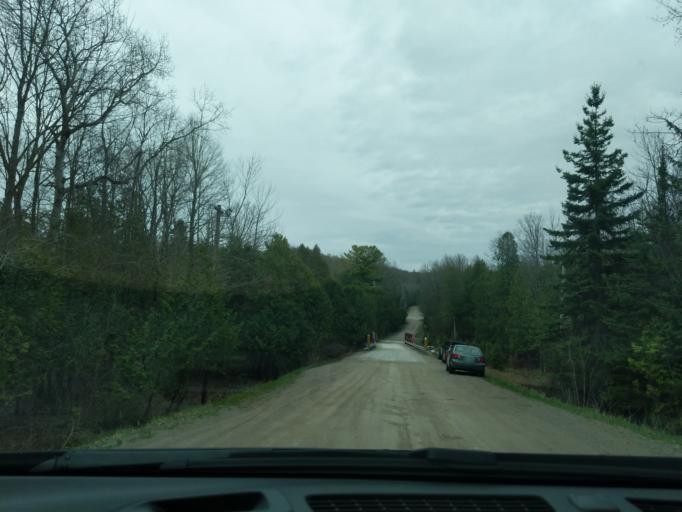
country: CA
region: Ontario
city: Orangeville
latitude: 43.9974
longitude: -80.0151
